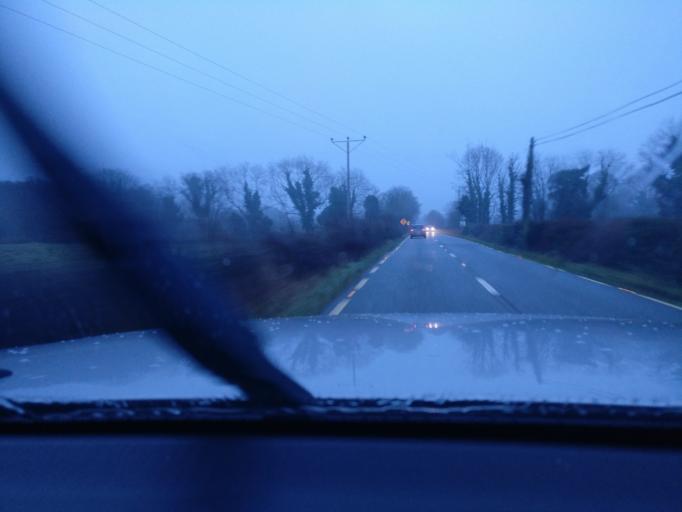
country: IE
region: Leinster
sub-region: An Mhi
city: Athboy
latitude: 53.6430
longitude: -6.8455
